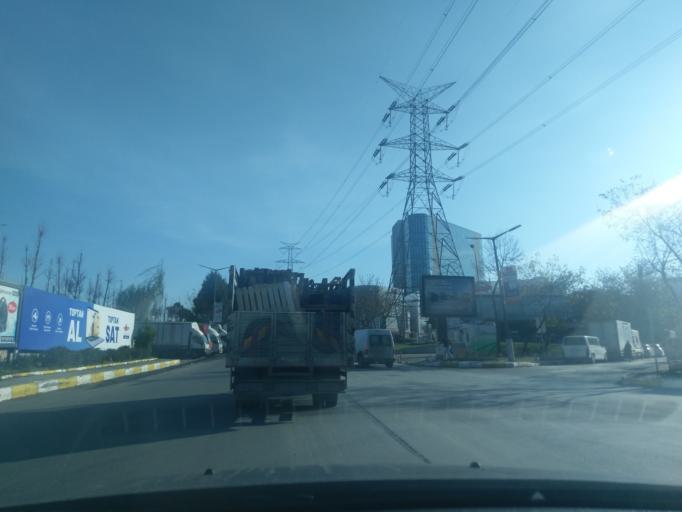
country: TR
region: Istanbul
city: Mahmutbey
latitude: 41.0699
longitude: 28.8256
